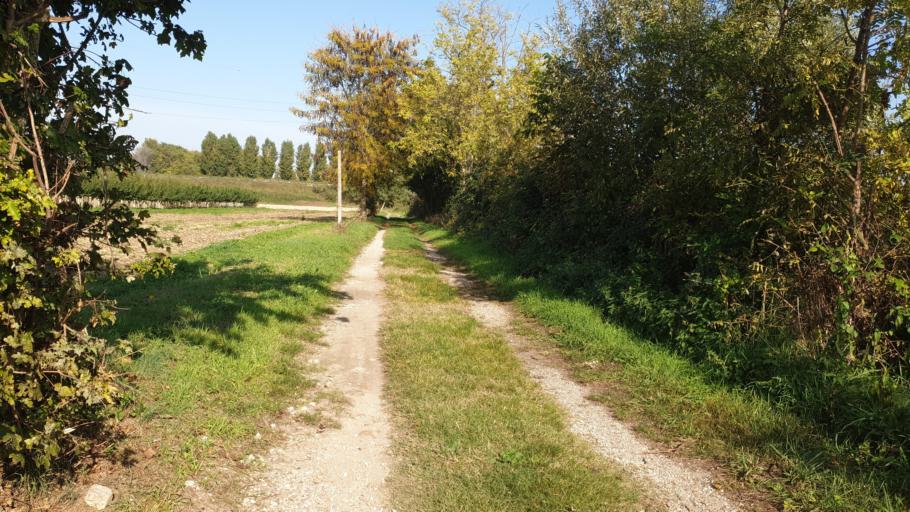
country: IT
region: Veneto
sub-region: Provincia di Venezia
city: Tombelle
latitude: 45.4059
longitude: 11.9696
